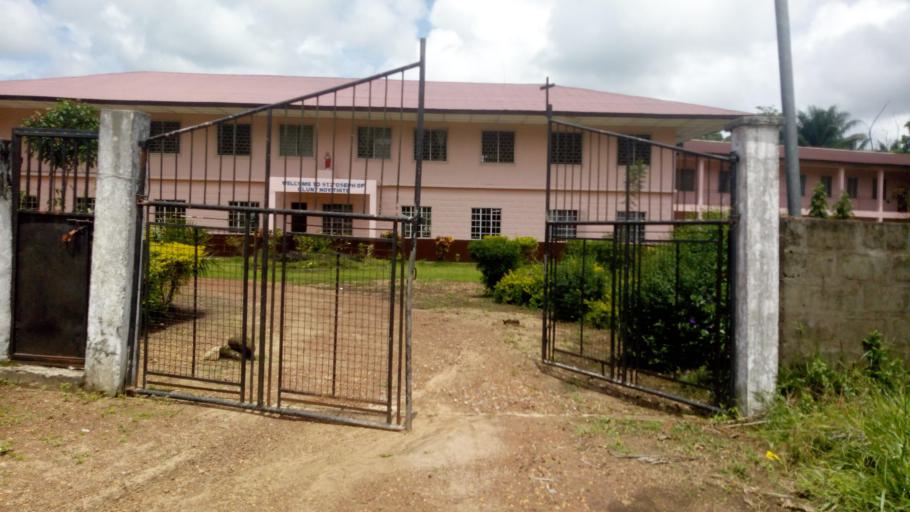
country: SL
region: Northern Province
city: Magburaka
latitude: 8.7146
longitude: -11.9517
